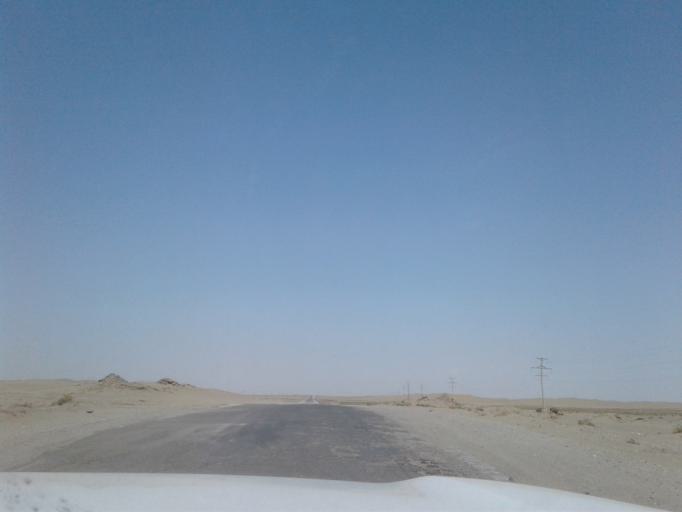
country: TM
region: Balkan
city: Gumdag
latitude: 38.3647
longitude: 54.3835
